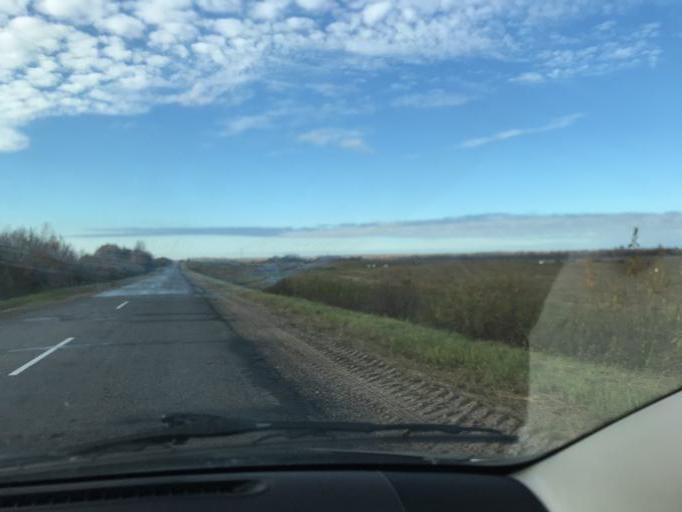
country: BY
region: Vitebsk
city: Haradok
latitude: 55.4136
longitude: 29.7652
